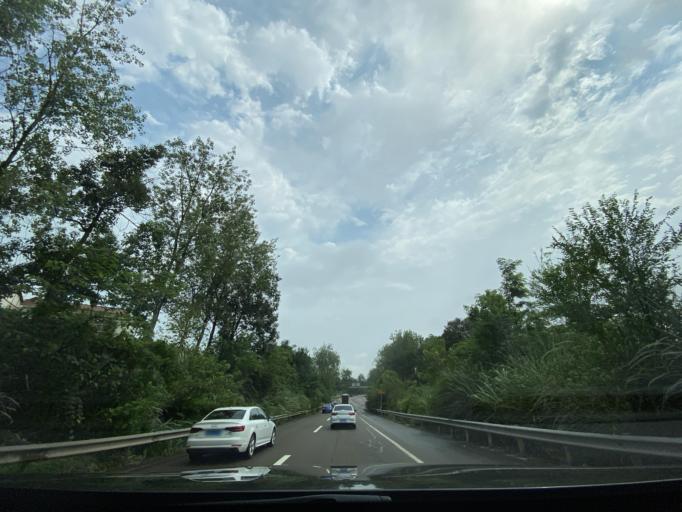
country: CN
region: Sichuan
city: Yanjiang
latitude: 29.9325
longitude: 104.6187
